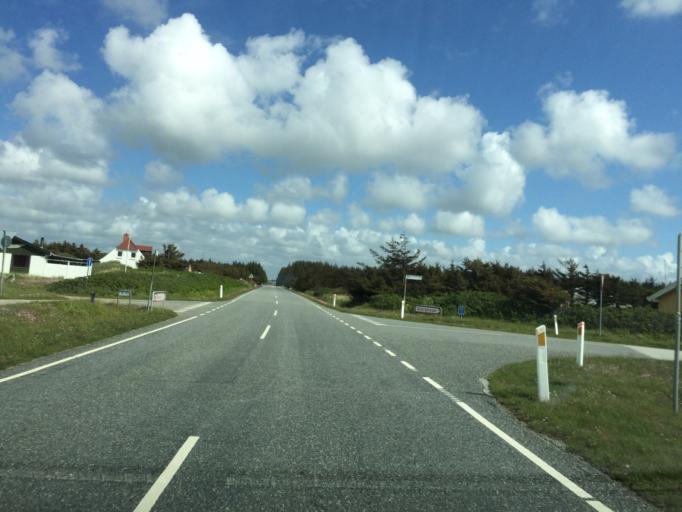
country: DK
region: Central Jutland
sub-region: Holstebro Kommune
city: Ulfborg
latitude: 56.3220
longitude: 8.1268
